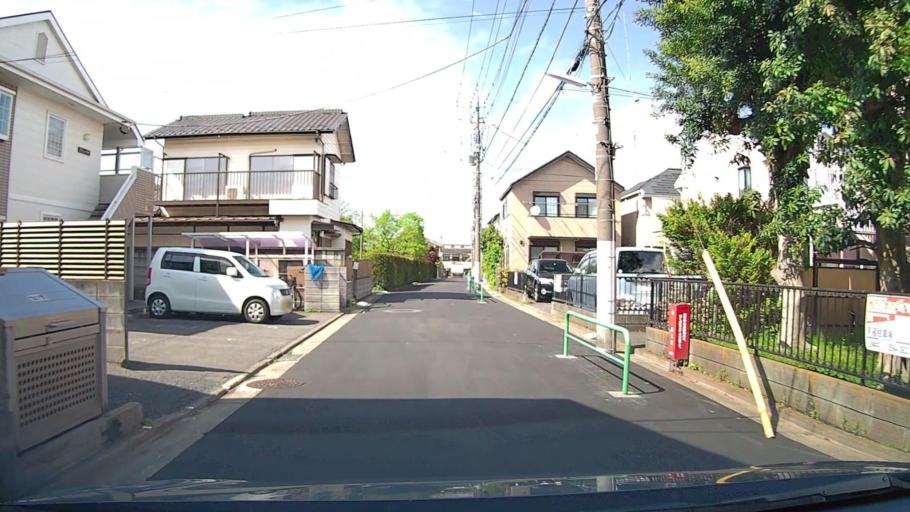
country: JP
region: Tokyo
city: Musashino
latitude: 35.7286
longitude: 139.5851
